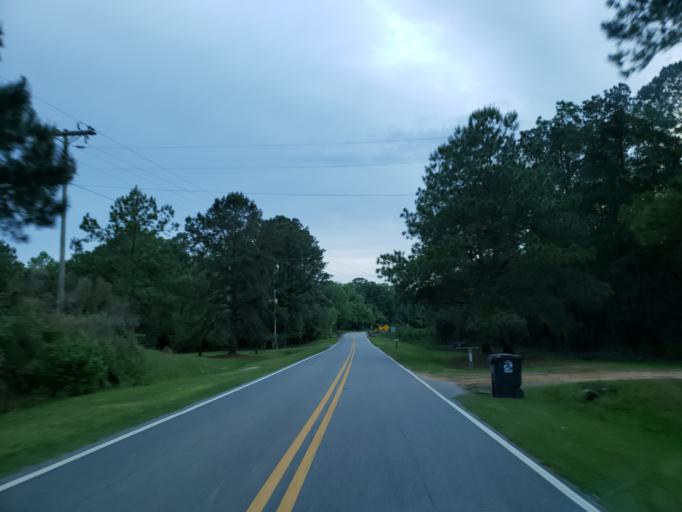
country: US
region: Georgia
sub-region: Lowndes County
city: Hahira
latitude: 30.9499
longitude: -83.3819
